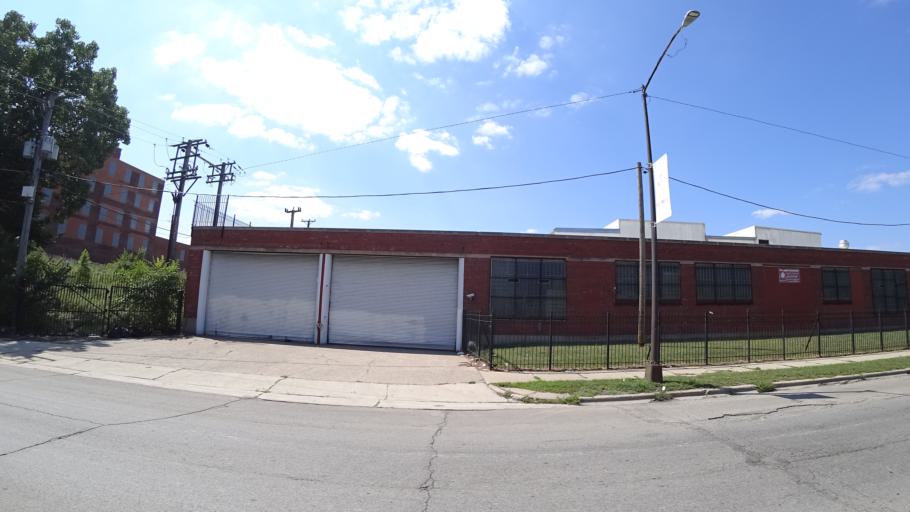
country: US
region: Illinois
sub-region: Cook County
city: Cicero
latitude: 41.8688
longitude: -87.7350
